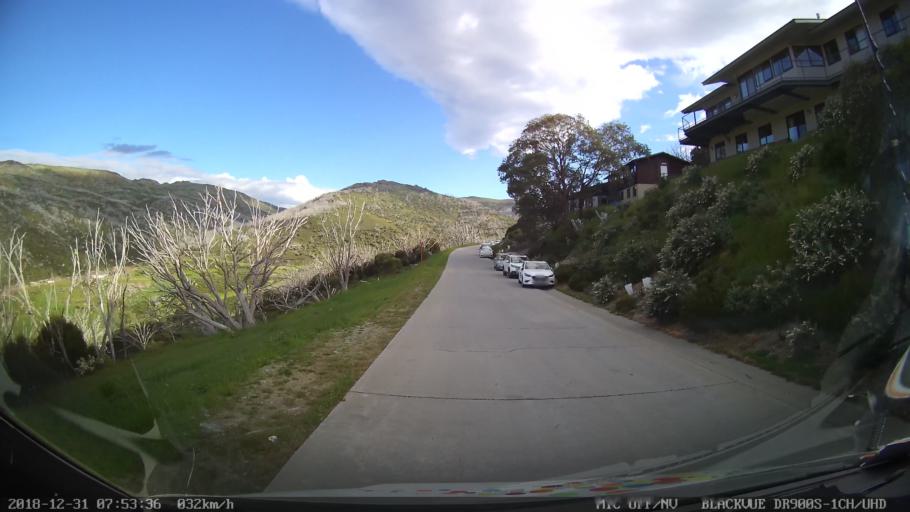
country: AU
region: New South Wales
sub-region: Snowy River
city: Jindabyne
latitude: -36.3799
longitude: 148.3739
